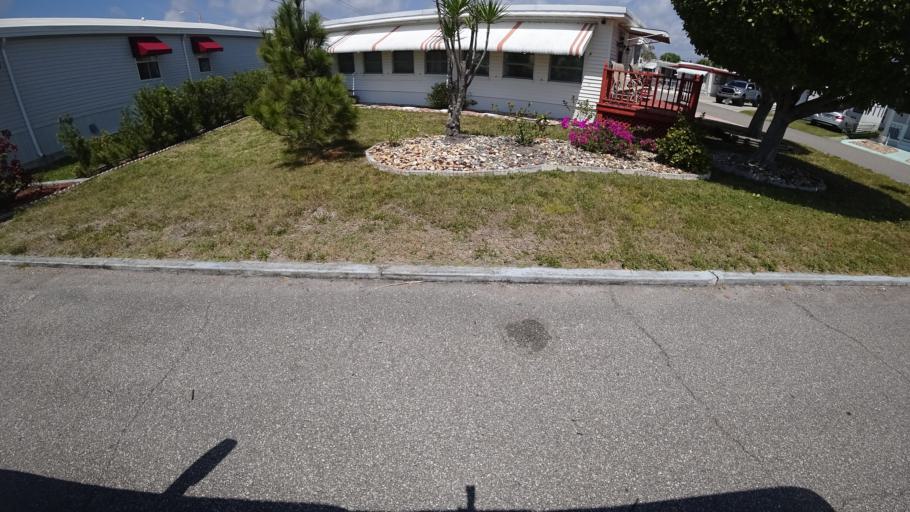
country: US
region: Florida
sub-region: Manatee County
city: Bayshore Gardens
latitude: 27.4244
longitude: -82.5830
